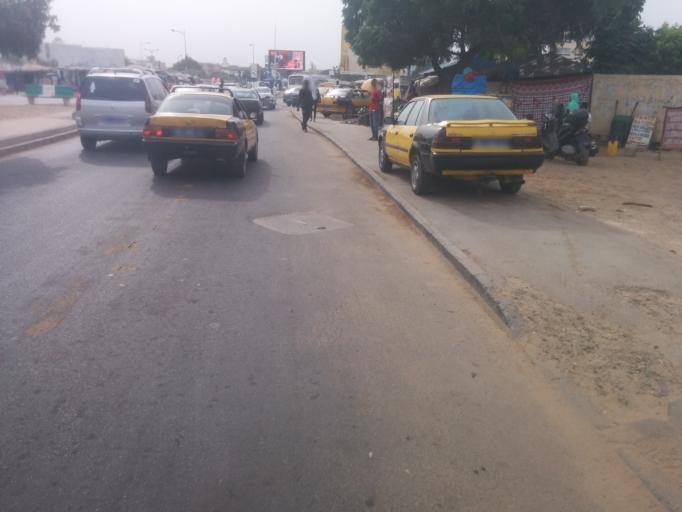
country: SN
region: Dakar
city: Grand Dakar
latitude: 14.7295
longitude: -17.4580
